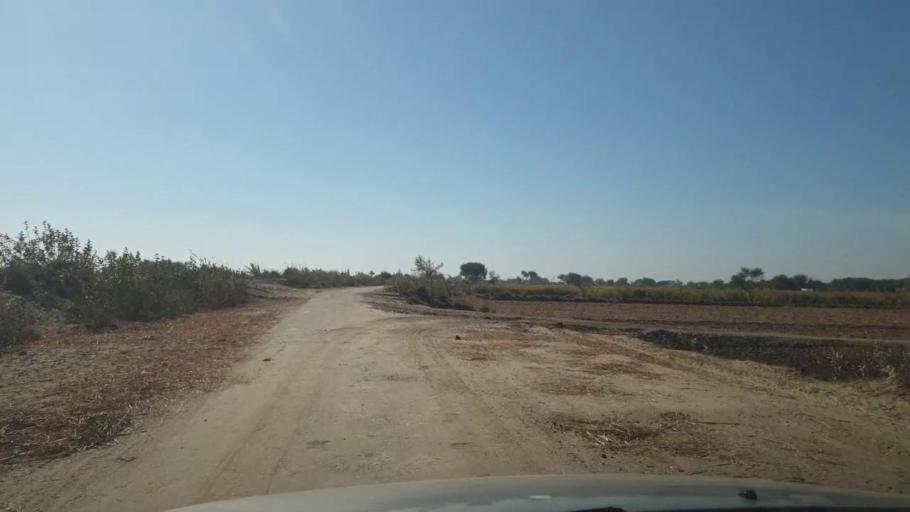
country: PK
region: Sindh
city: Ghotki
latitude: 28.0198
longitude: 69.2679
